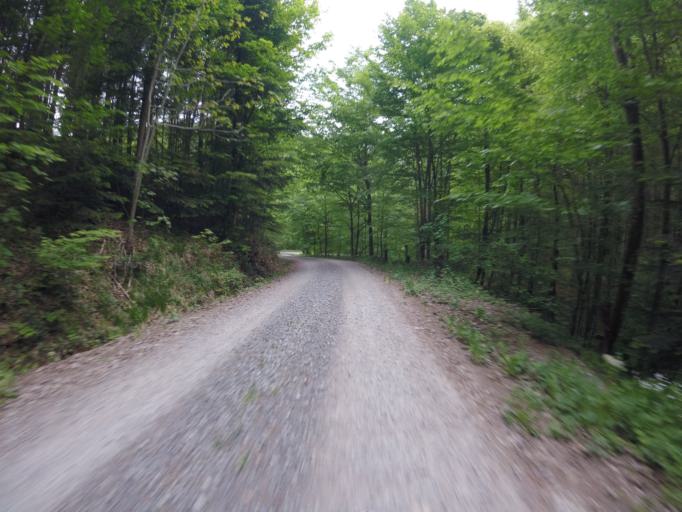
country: DE
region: Baden-Wuerttemberg
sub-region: Regierungsbezirk Stuttgart
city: Spiegelberg
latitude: 49.0169
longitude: 9.4385
